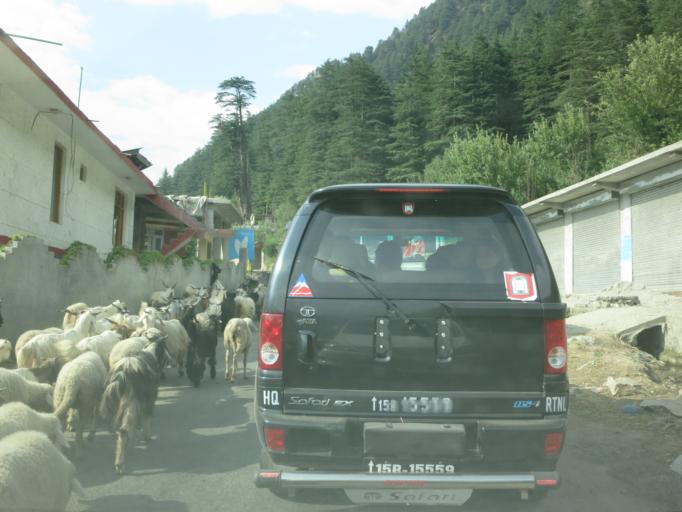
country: IN
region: Himachal Pradesh
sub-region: Kulu
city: Nagar
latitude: 32.1657
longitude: 77.1920
